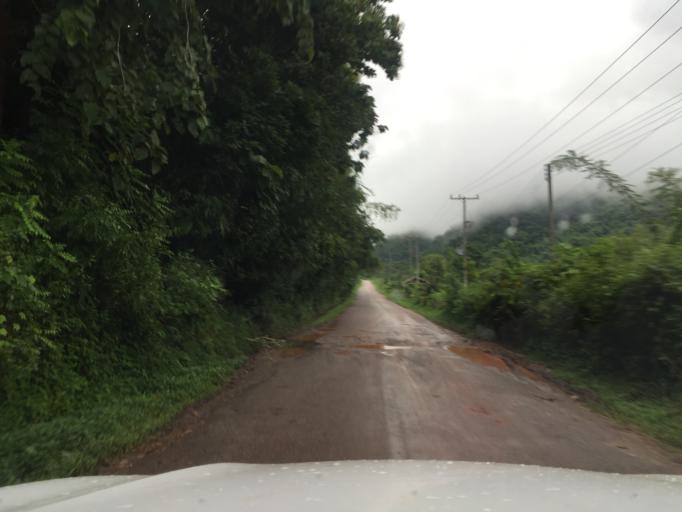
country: LA
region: Oudomxai
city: Muang La
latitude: 20.8361
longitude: 102.1022
